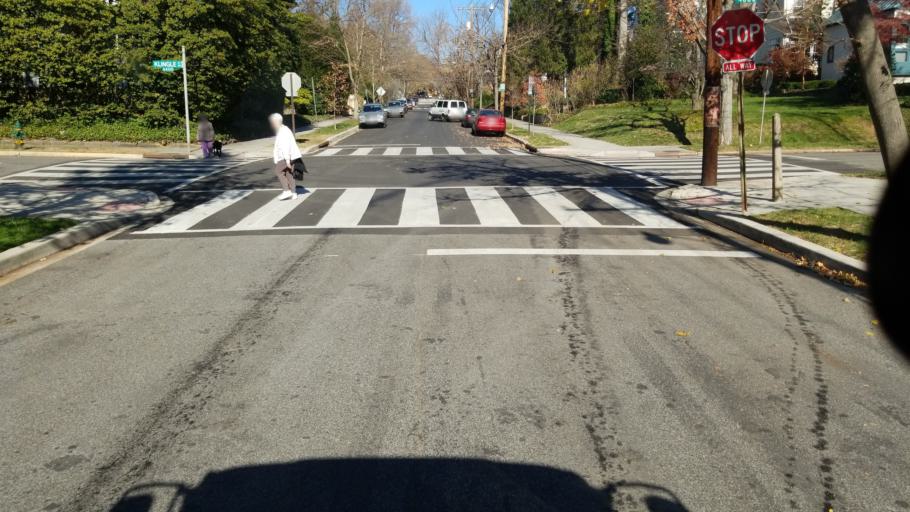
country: US
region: Maryland
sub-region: Montgomery County
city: Friendship Village
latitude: 38.9312
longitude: -77.0862
